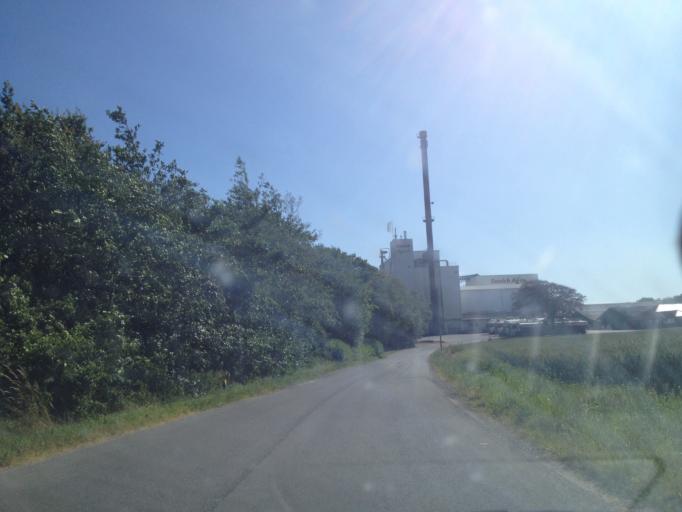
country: DK
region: South Denmark
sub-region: Kolding Kommune
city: Christiansfeld
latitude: 55.4017
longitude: 9.5254
